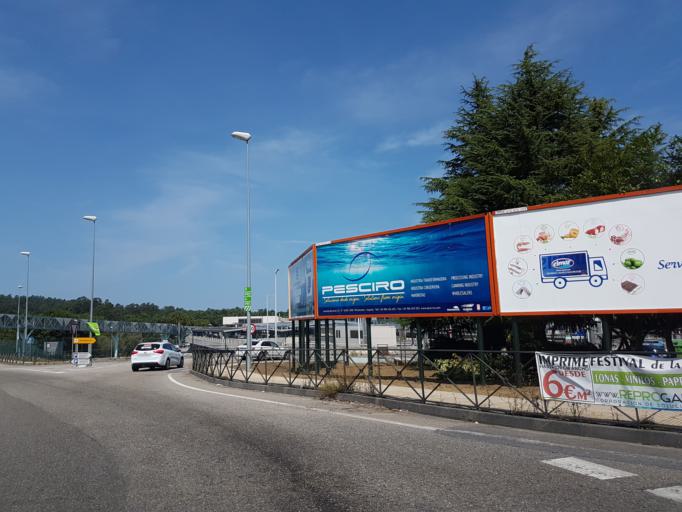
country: ES
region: Galicia
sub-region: Provincia de Pontevedra
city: Porrino
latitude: 42.2233
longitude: -8.6347
